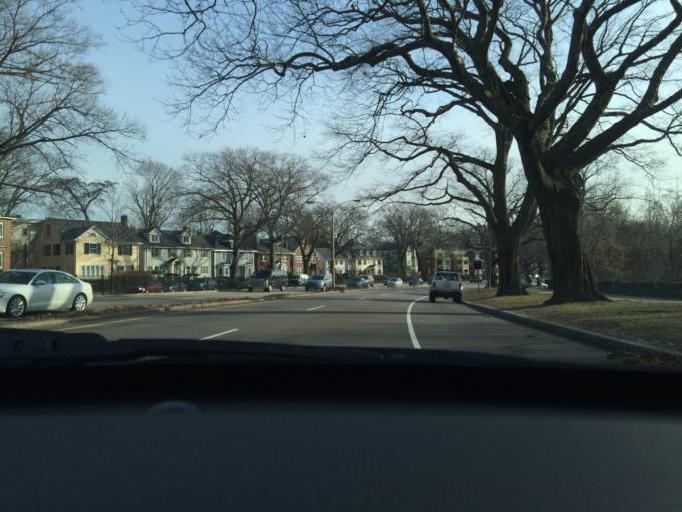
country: US
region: Massachusetts
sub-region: Suffolk County
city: Jamaica Plain
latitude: 42.3087
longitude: -71.1206
